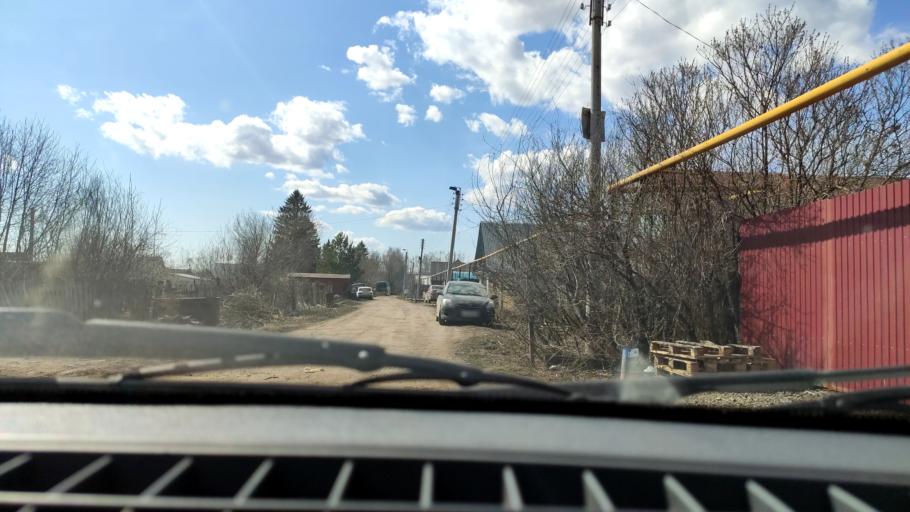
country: RU
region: Bashkortostan
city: Avdon
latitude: 54.6790
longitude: 55.8168
